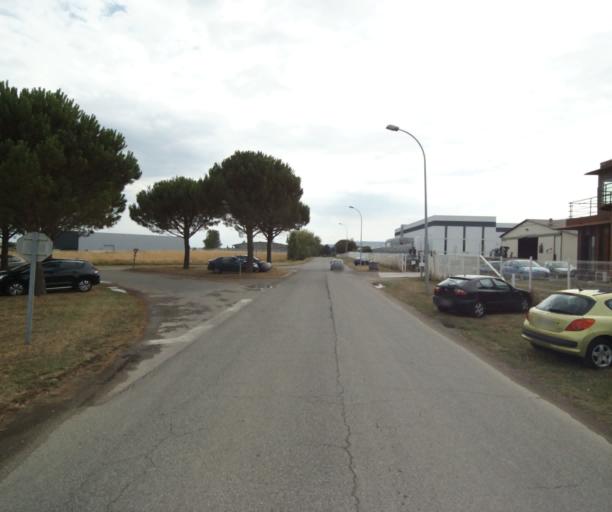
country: FR
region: Midi-Pyrenees
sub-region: Departement de la Haute-Garonne
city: Revel
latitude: 43.4547
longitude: 1.9747
